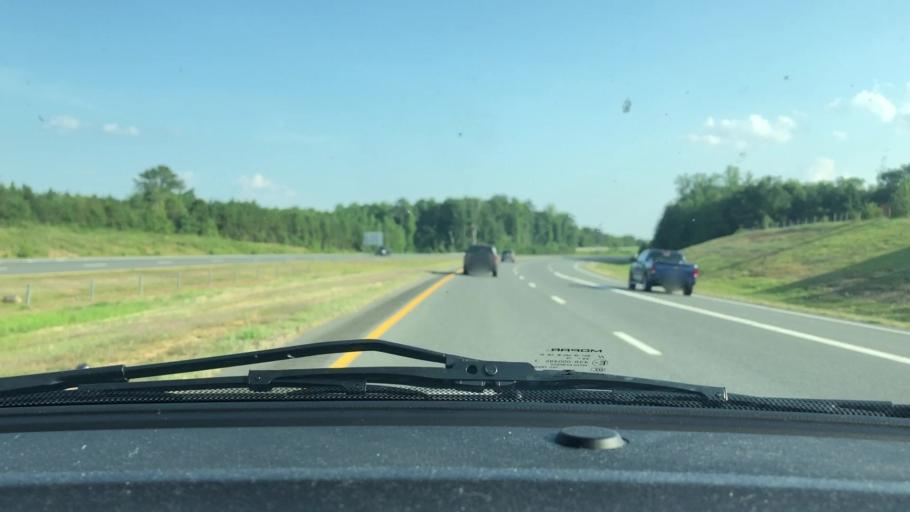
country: US
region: North Carolina
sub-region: Lee County
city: Broadway
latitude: 35.4418
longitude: -79.1193
